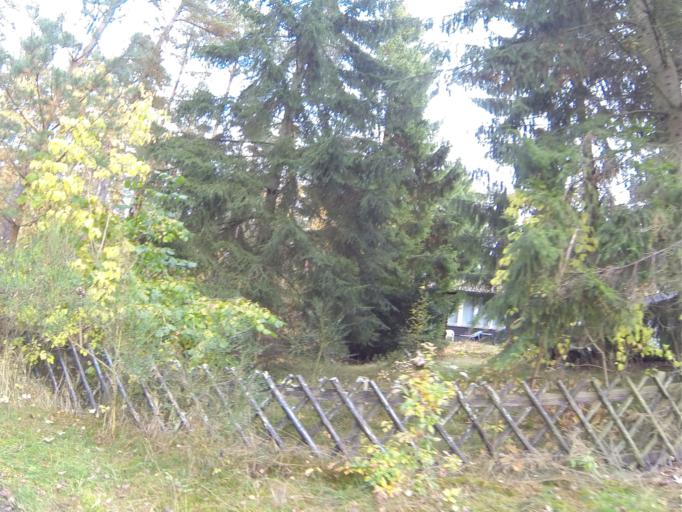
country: SE
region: Skane
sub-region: Sjobo Kommun
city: Blentarp
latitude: 55.6327
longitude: 13.6369
